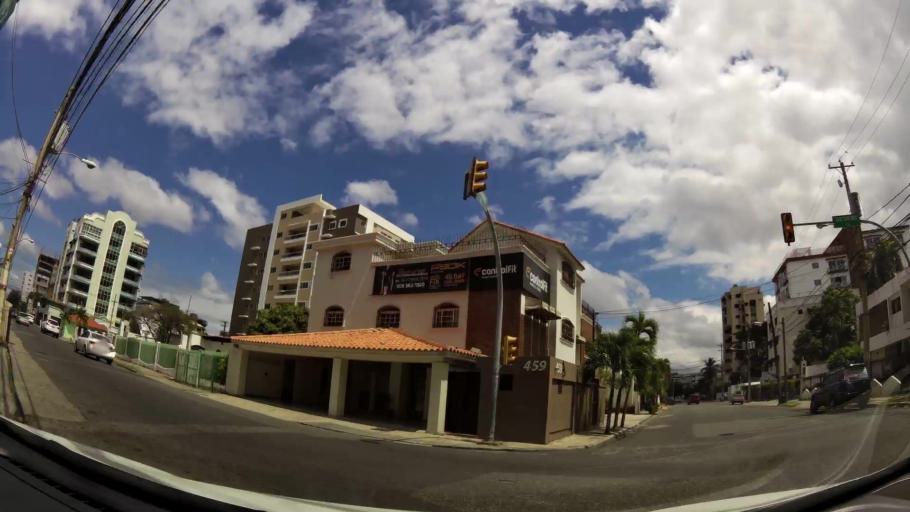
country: DO
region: Nacional
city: Bella Vista
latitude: 18.4609
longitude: -69.9454
